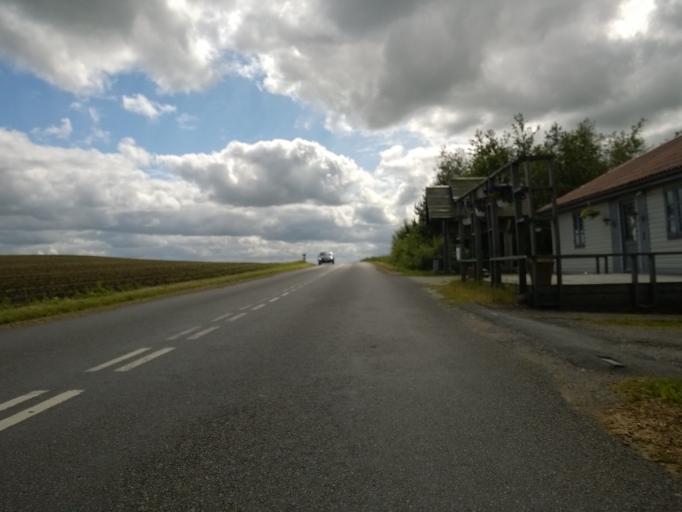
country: DK
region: Central Jutland
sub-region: Holstebro Kommune
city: Vinderup
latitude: 56.4259
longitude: 8.8470
